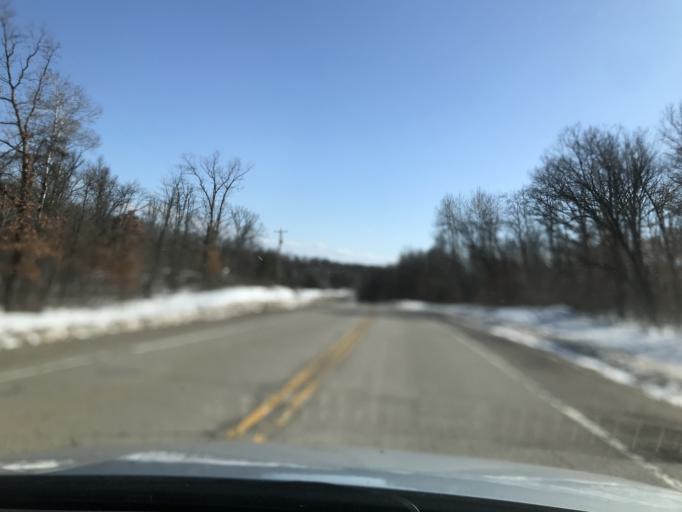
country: US
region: Wisconsin
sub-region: Marinette County
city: Niagara
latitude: 45.3407
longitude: -88.1016
